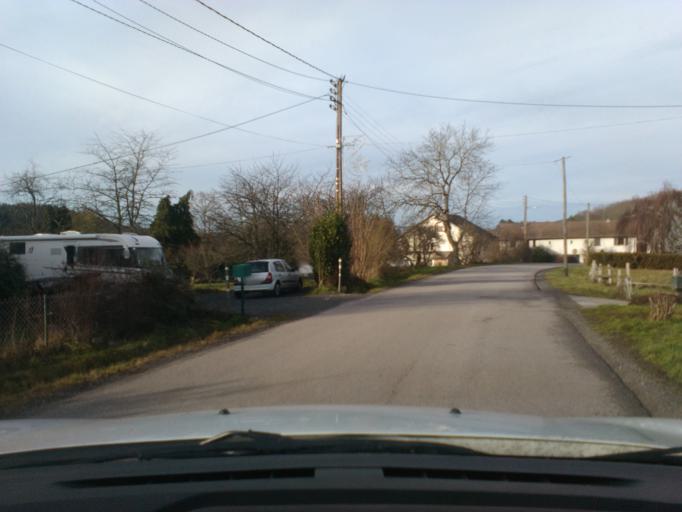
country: FR
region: Lorraine
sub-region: Departement des Vosges
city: Fraize
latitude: 48.1729
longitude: 6.9791
